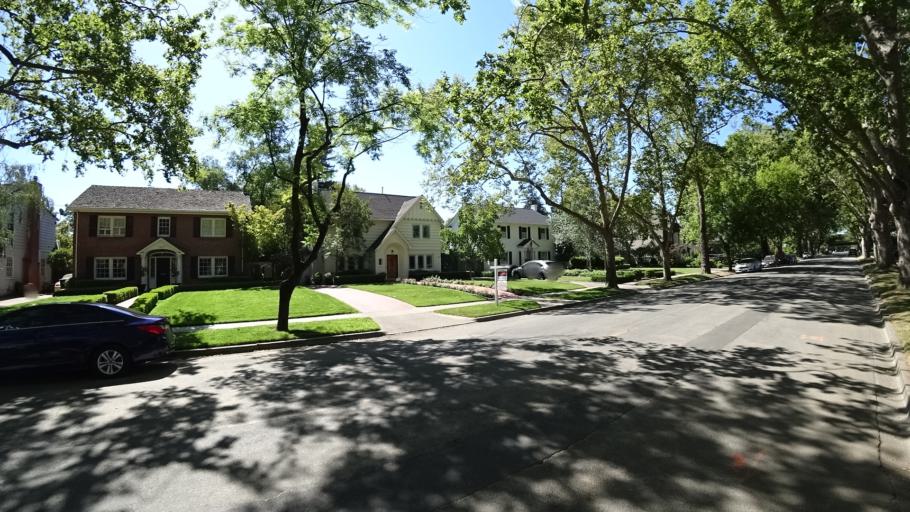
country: US
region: California
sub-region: Sacramento County
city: Sacramento
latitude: 38.5628
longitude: -121.4571
